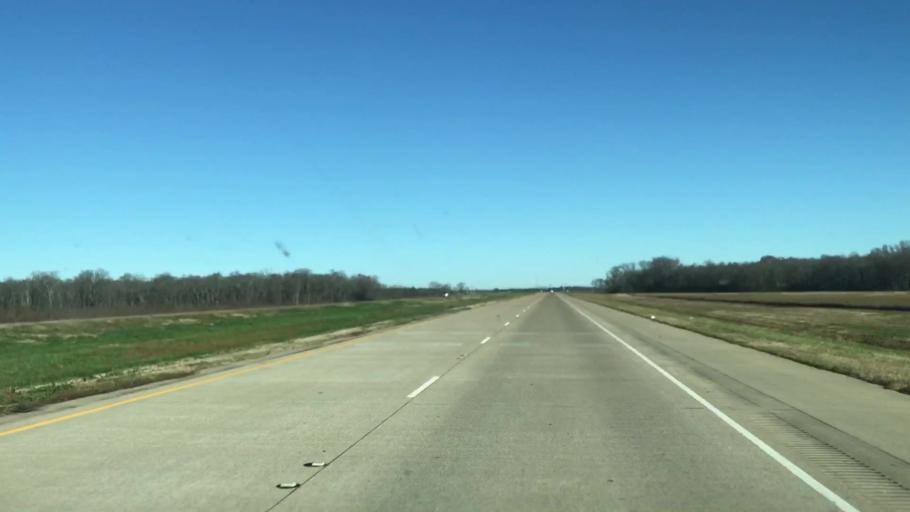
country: US
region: Louisiana
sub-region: Caddo Parish
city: Blanchard
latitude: 32.6385
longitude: -93.8382
